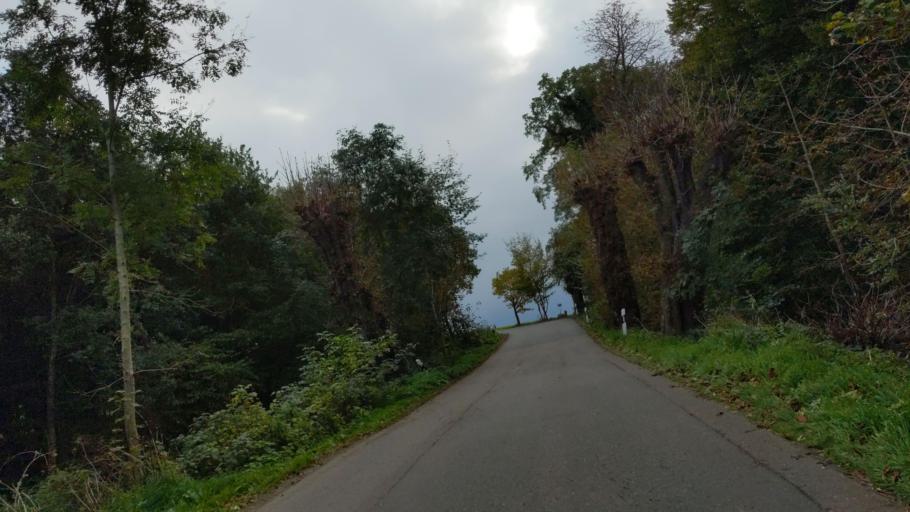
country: DE
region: Schleswig-Holstein
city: Sierksdorf
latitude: 54.0854
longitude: 10.7453
